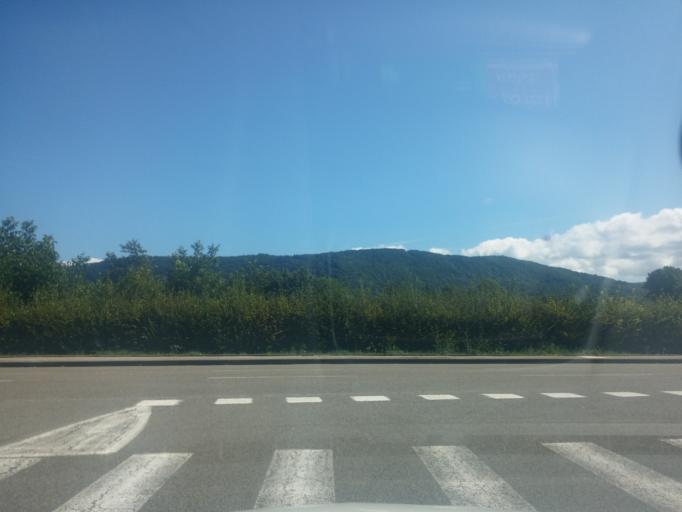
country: FR
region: Franche-Comte
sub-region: Departement du Jura
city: Saint-Lupicin
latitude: 46.4058
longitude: 5.7939
